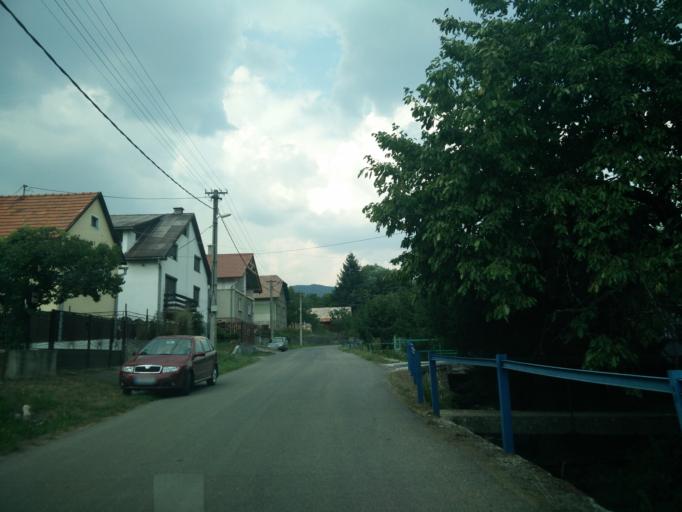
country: SK
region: Banskobystricky
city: Zarnovica
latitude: 48.6042
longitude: 18.7098
